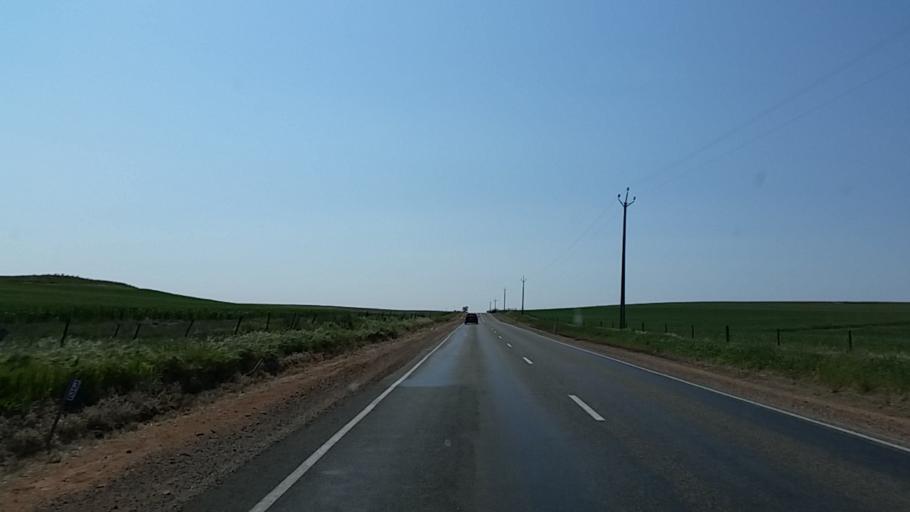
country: AU
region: South Australia
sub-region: Northern Areas
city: Jamestown
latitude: -33.1968
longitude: 138.4471
